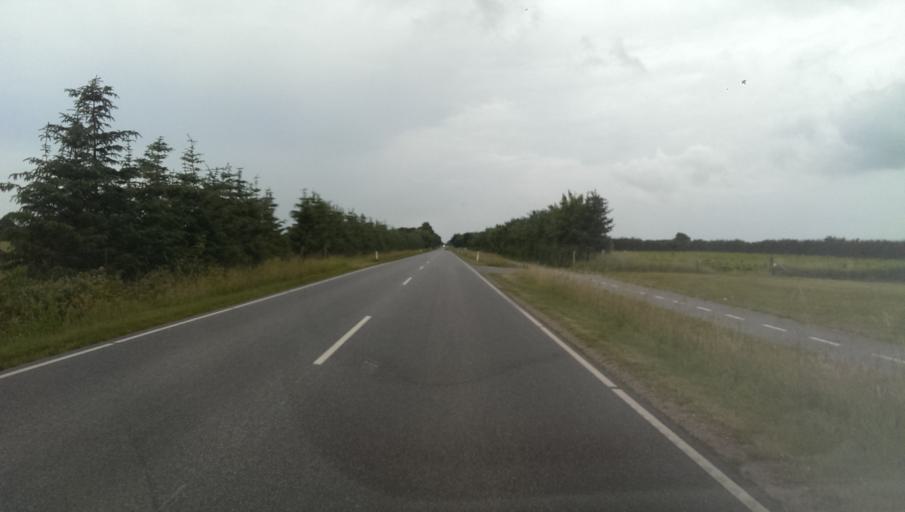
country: DK
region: South Denmark
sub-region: Esbjerg Kommune
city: Bramming
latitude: 55.4573
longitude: 8.7140
